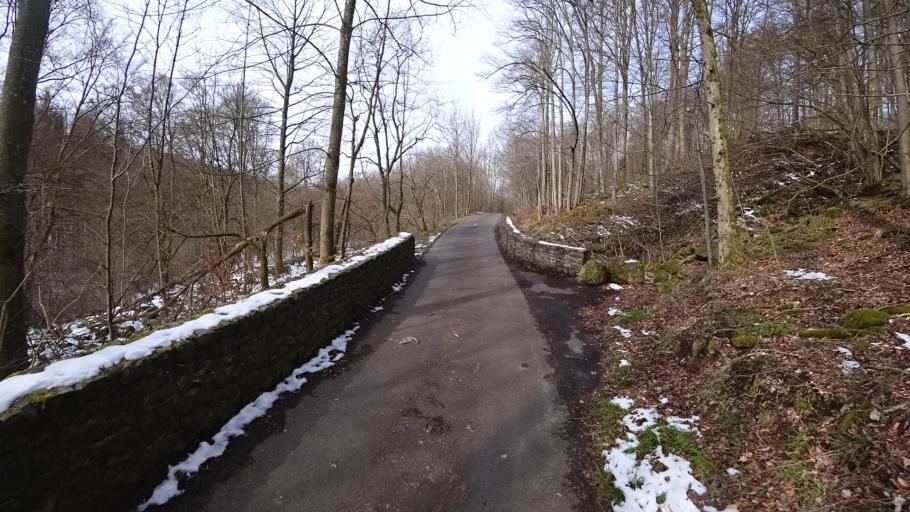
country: DE
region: Rheinland-Pfalz
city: Nauroth
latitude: 50.6882
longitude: 7.8705
